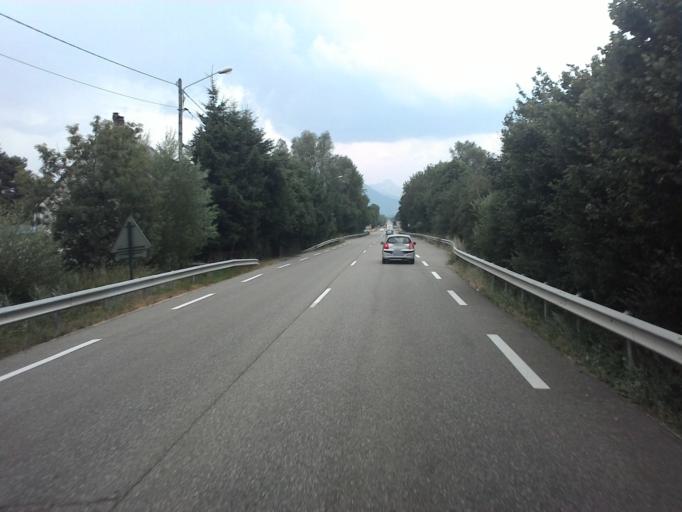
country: FR
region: Rhone-Alpes
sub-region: Departement de l'Isere
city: Pierre-Chatel
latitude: 44.9384
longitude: 5.7808
